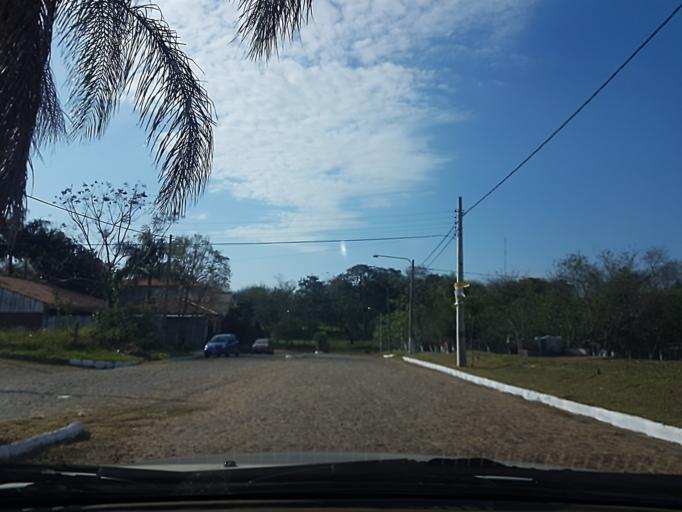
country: PY
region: Central
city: Colonia Mariano Roque Alonso
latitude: -25.2454
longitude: -57.5379
